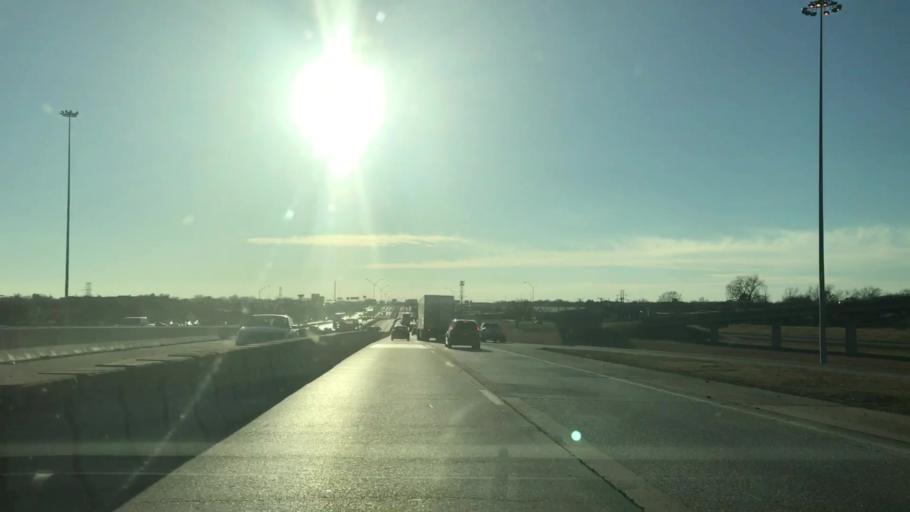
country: US
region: Texas
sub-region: Dallas County
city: Mesquite
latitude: 32.8227
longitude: -96.6307
